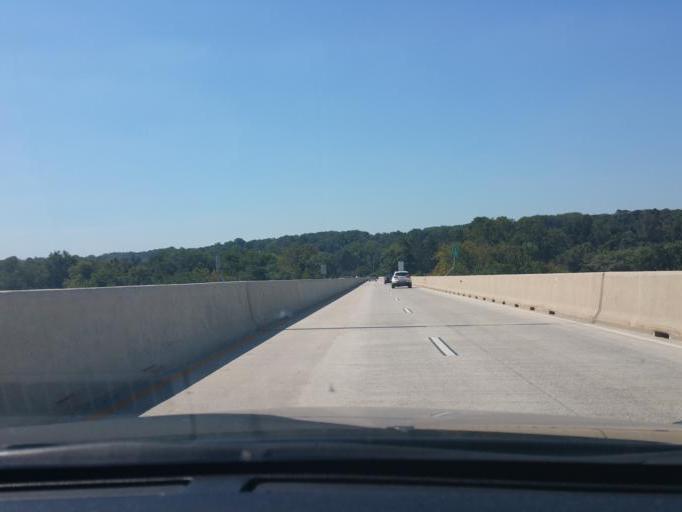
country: US
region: Maryland
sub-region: Harford County
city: Havre de Grace
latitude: 39.5590
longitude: -76.0938
